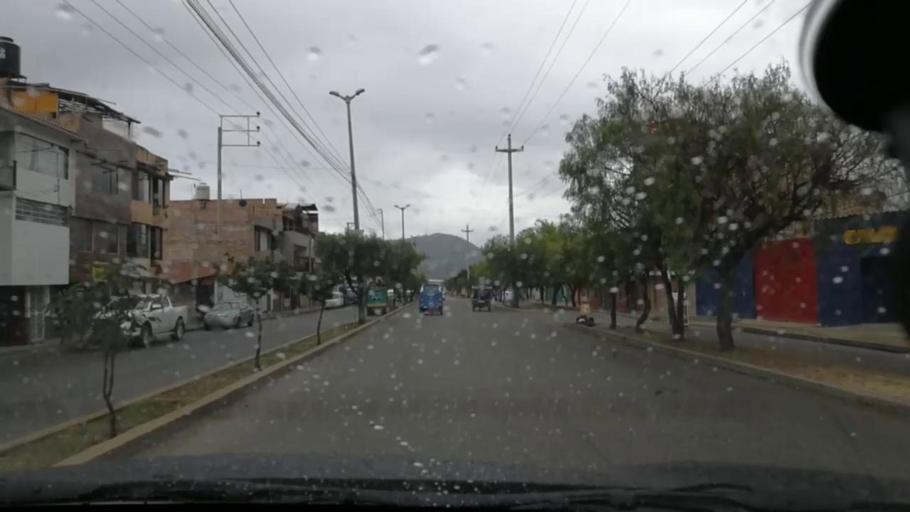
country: PE
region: Cajamarca
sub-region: Provincia de Cajamarca
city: Cajamarca
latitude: -7.1656
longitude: -78.5000
